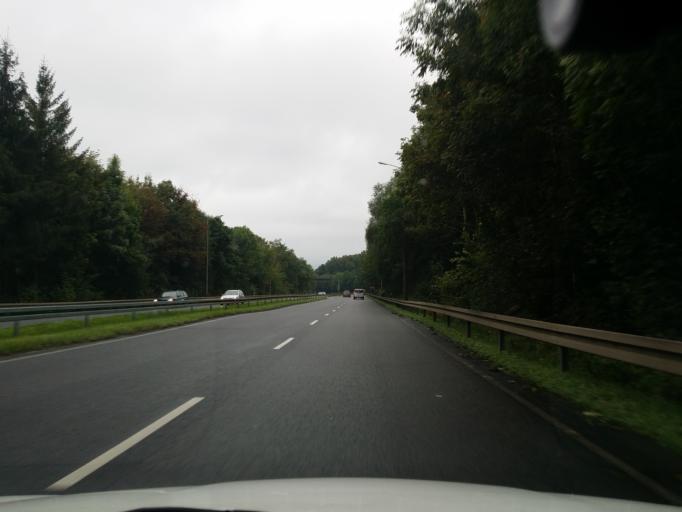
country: DE
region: Saxony
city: Leipzig
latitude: 51.3090
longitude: 12.3654
